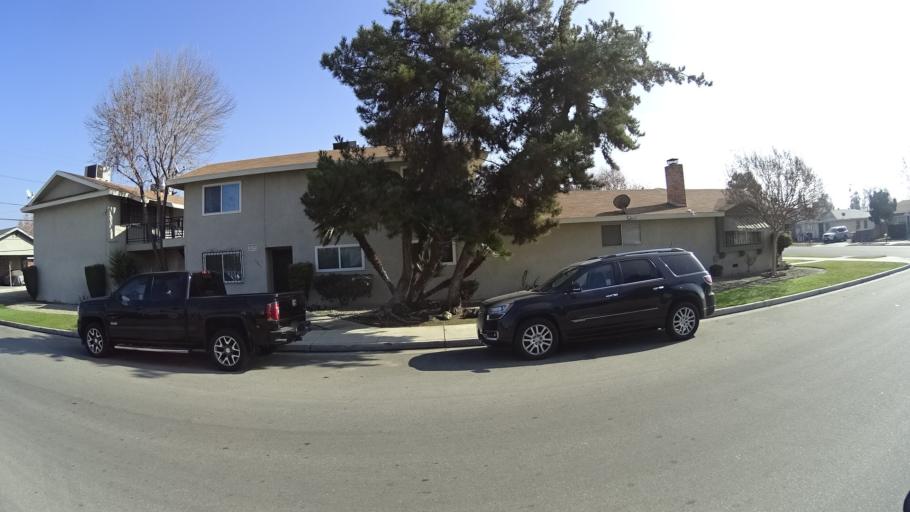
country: US
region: California
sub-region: Kern County
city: Bakersfield
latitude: 35.3891
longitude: -118.9902
